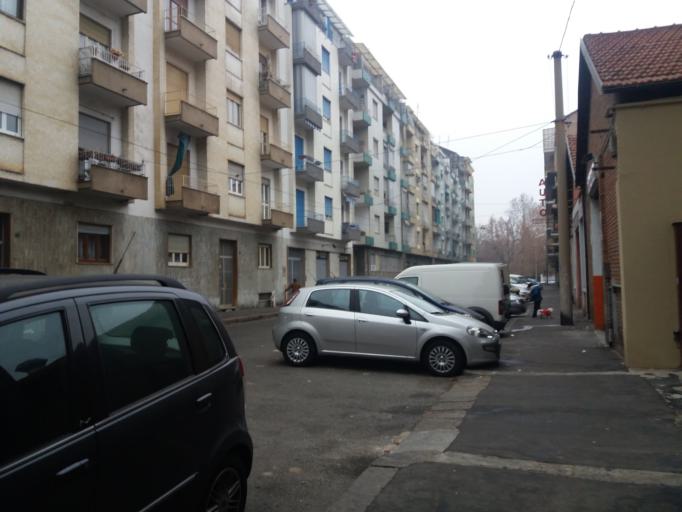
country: IT
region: Piedmont
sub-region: Provincia di Torino
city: Lesna
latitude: 45.0634
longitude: 7.6208
